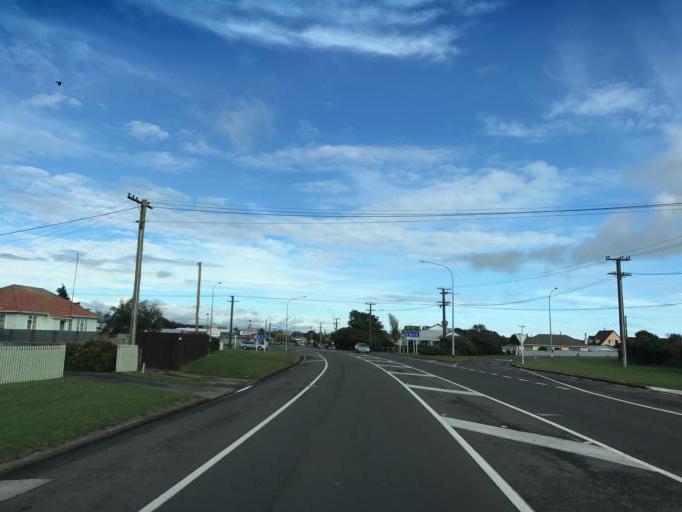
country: NZ
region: Manawatu-Wanganui
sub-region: Horowhenua District
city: Foxton
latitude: -40.4707
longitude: 175.2861
